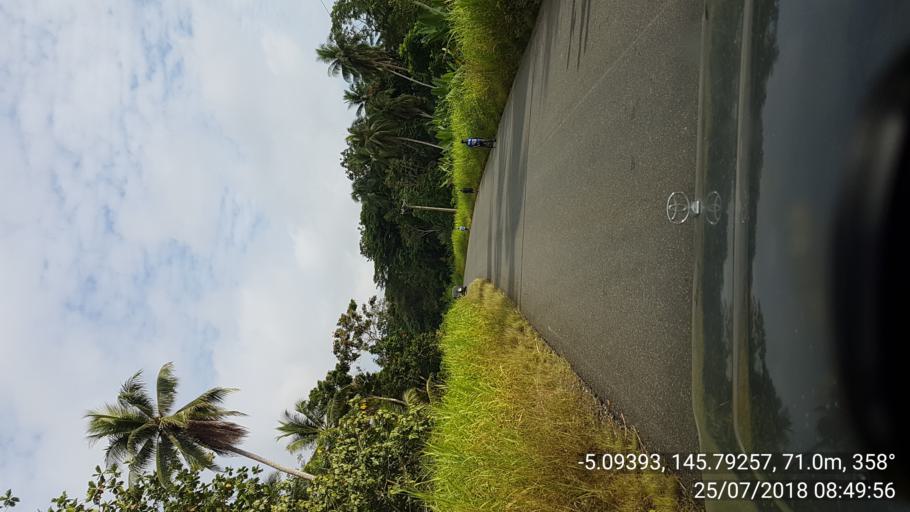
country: PG
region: Madang
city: Madang
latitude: -5.0942
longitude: 145.7928
